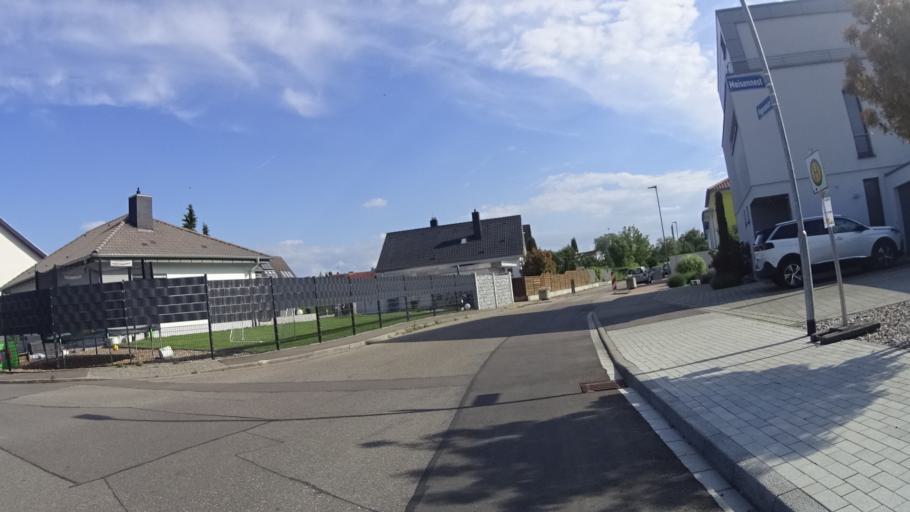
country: DE
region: Baden-Wuerttemberg
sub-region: Freiburg Region
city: Breisach am Rhein
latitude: 48.0410
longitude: 7.5846
